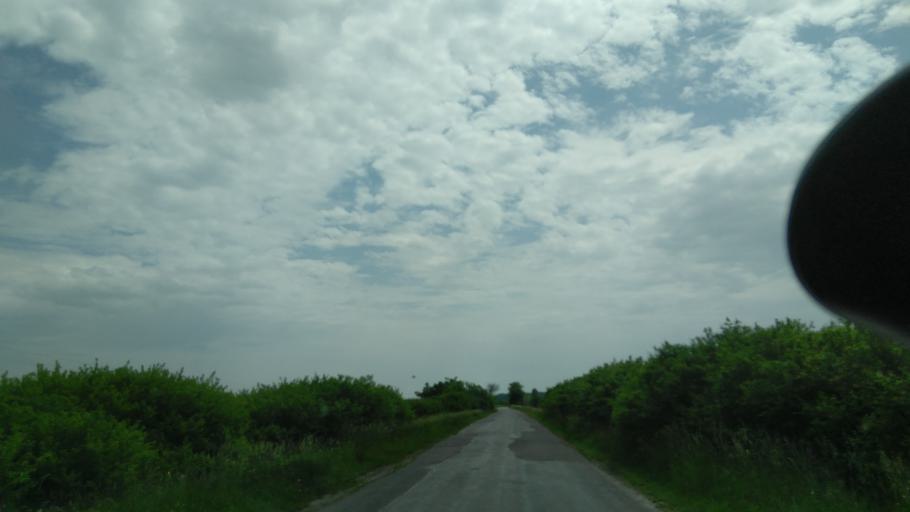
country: RO
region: Bihor
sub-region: Comuna Sannicolau-Roman
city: Sannicolau Roman
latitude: 47.0055
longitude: 21.6135
